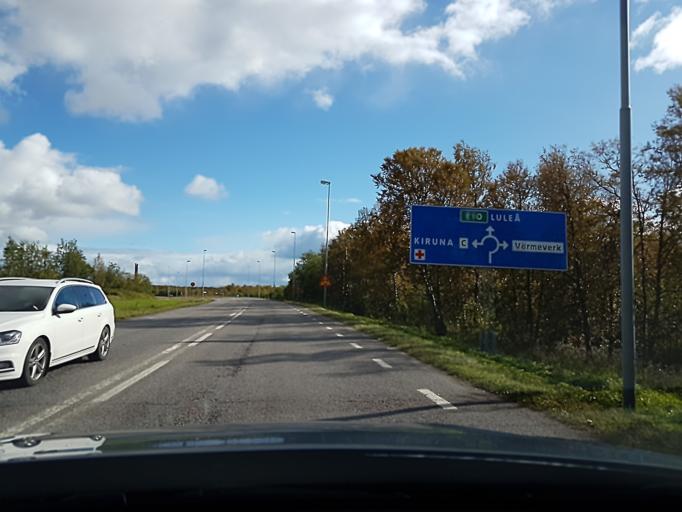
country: SE
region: Norrbotten
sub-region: Kiruna Kommun
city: Kiruna
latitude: 67.8446
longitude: 20.2255
